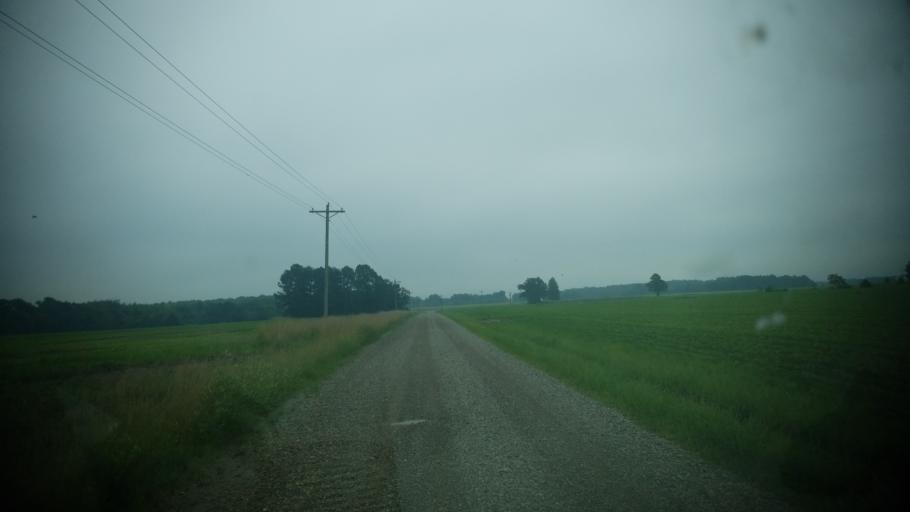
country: US
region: Illinois
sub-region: Clay County
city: Flora
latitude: 38.5881
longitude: -88.3695
